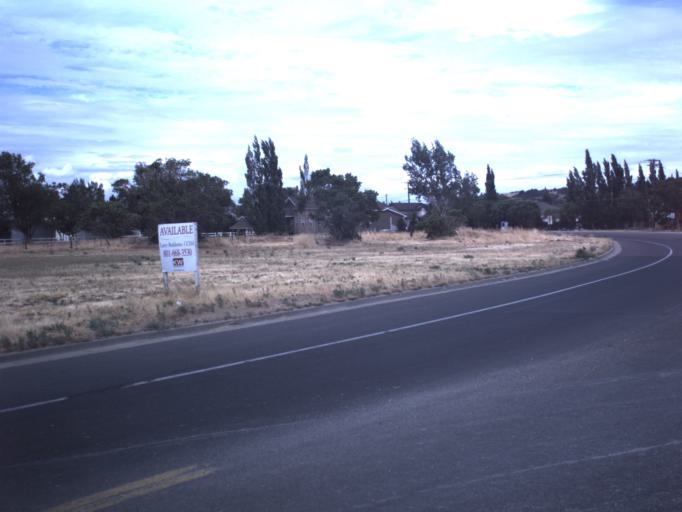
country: US
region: Utah
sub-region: Davis County
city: South Weber
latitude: 41.1310
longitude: -111.9240
